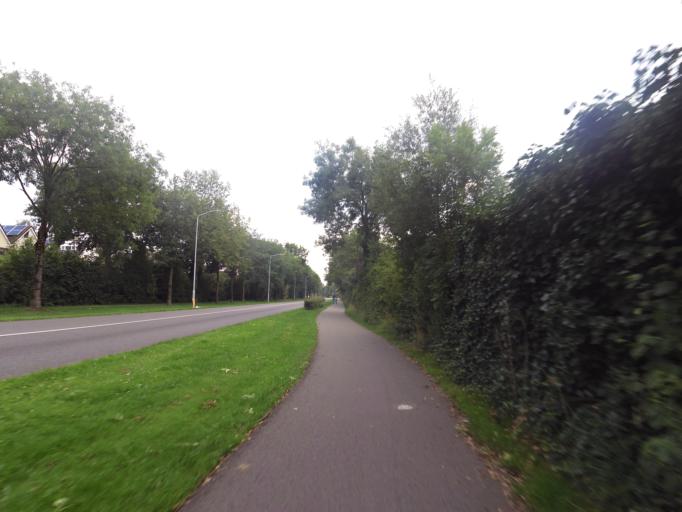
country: NL
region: Gelderland
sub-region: Oude IJsselstreek
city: Gendringen
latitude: 51.8863
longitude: 6.3760
